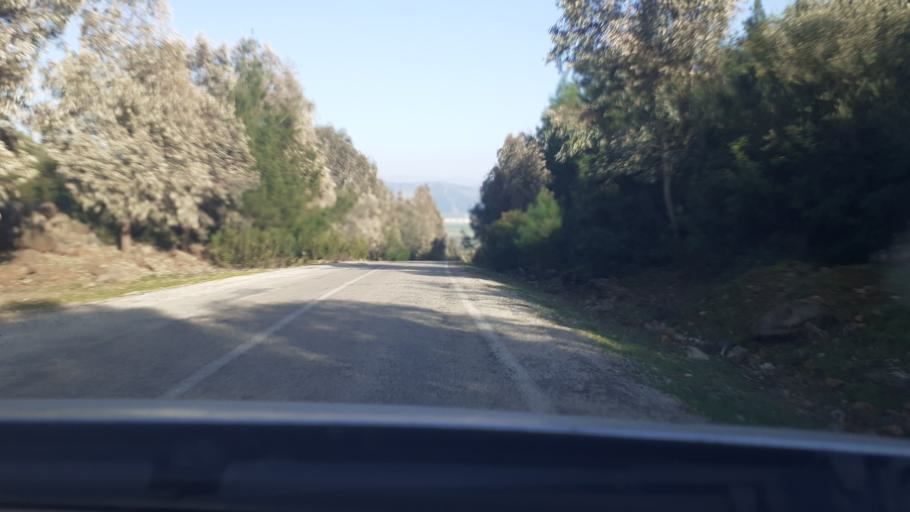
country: TR
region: Hatay
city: Aktepe
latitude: 36.7328
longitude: 36.4745
